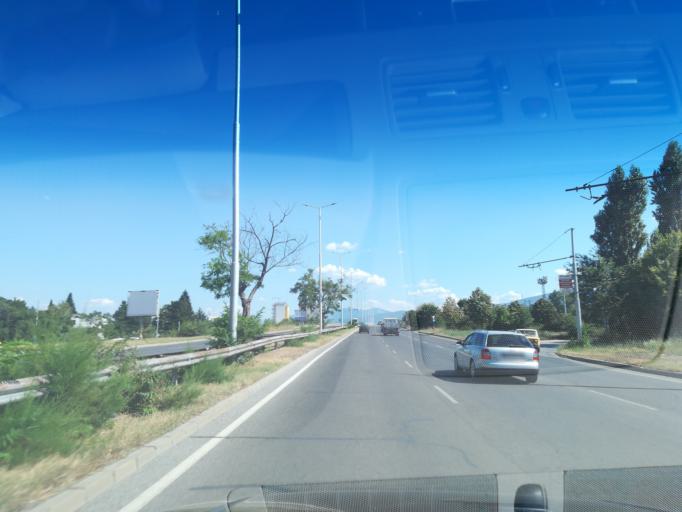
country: BG
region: Plovdiv
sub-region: Obshtina Plovdiv
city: Plovdiv
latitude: 42.1207
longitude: 24.7746
